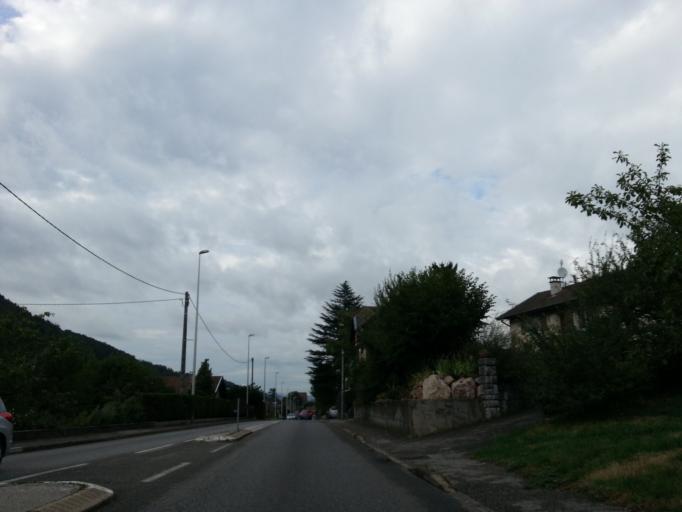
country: FR
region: Rhone-Alpes
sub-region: Departement de la Haute-Savoie
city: Sevrier
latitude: 45.8705
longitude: 6.1408
